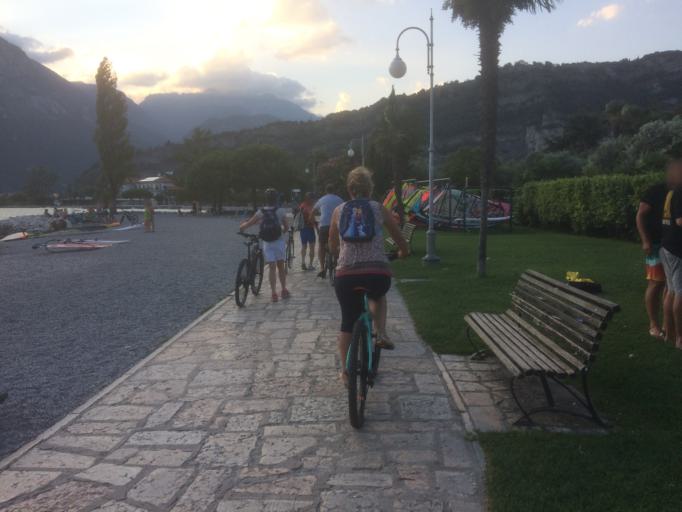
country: IT
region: Trentino-Alto Adige
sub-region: Provincia di Trento
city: Torbole sul Garda
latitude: 45.8712
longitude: 10.8708
